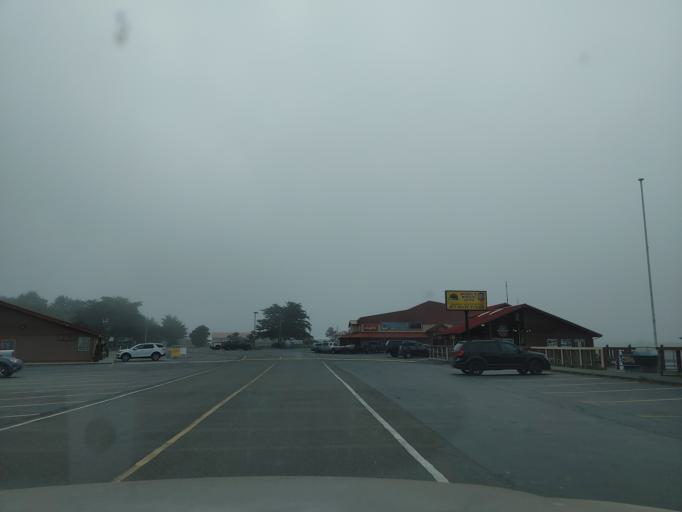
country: US
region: Oregon
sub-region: Curry County
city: Gold Beach
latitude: 42.4218
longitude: -124.4178
